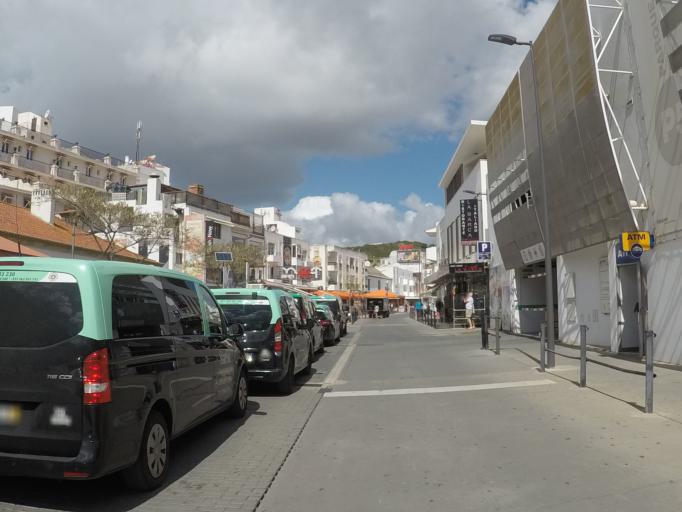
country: PT
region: Faro
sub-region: Albufeira
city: Albufeira
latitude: 37.0997
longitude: -8.2393
